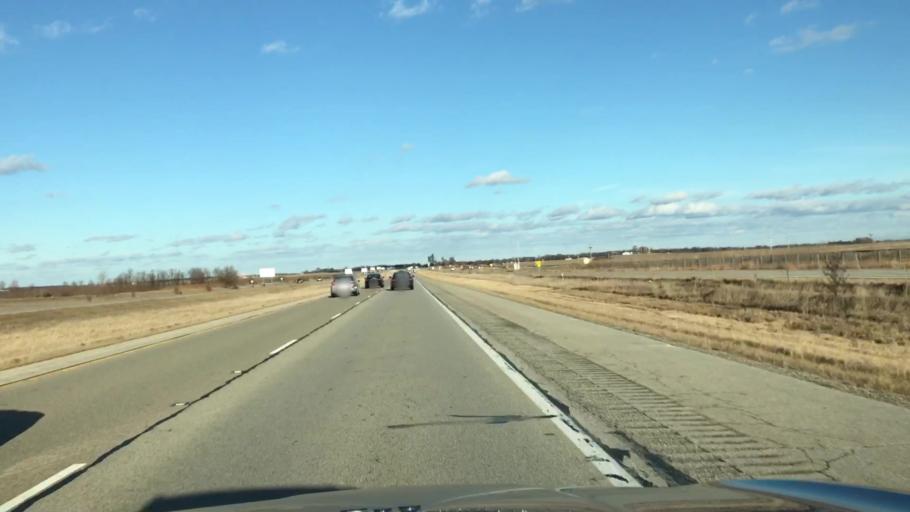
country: US
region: Illinois
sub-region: McLean County
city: Normal
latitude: 40.5448
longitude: -88.9291
